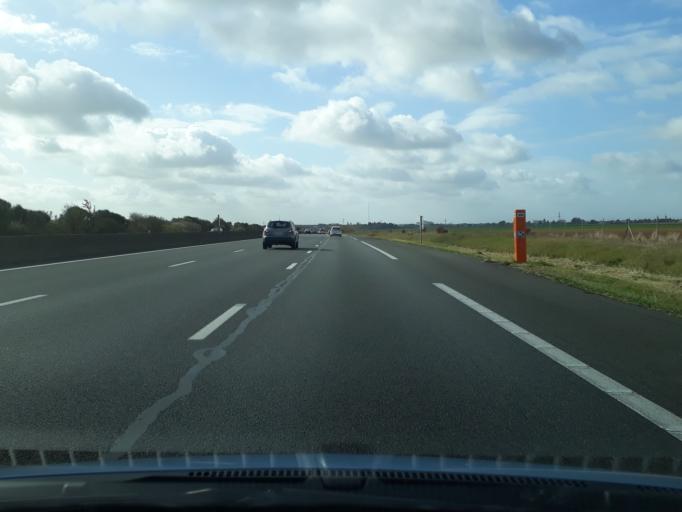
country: FR
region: Centre
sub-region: Departement du Loir-et-Cher
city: La Chaussee-Saint-Victor
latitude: 47.6389
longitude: 1.3598
